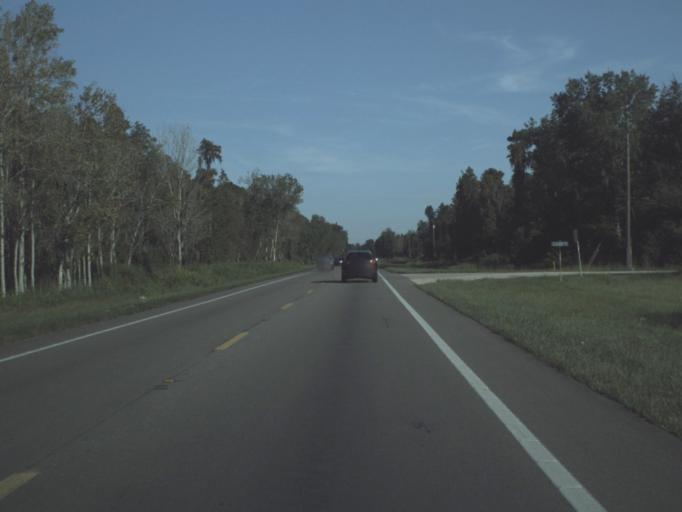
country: US
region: Florida
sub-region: Polk County
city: Kathleen
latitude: 28.1970
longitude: -82.0030
